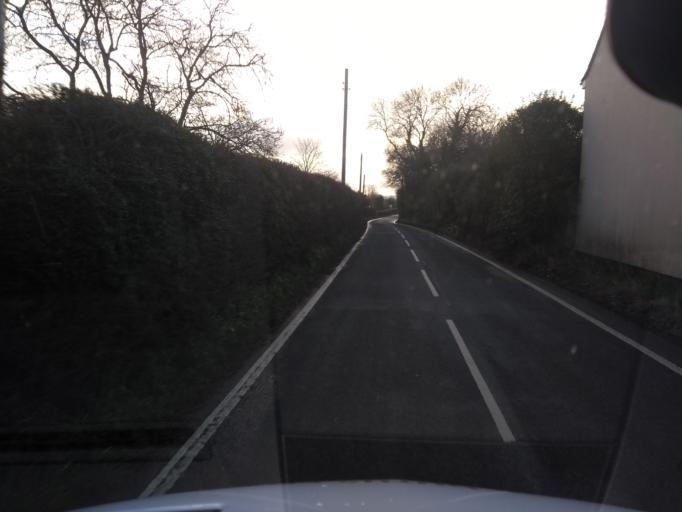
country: GB
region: England
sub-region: Somerset
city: Wedmore
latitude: 51.2249
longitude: -2.7983
